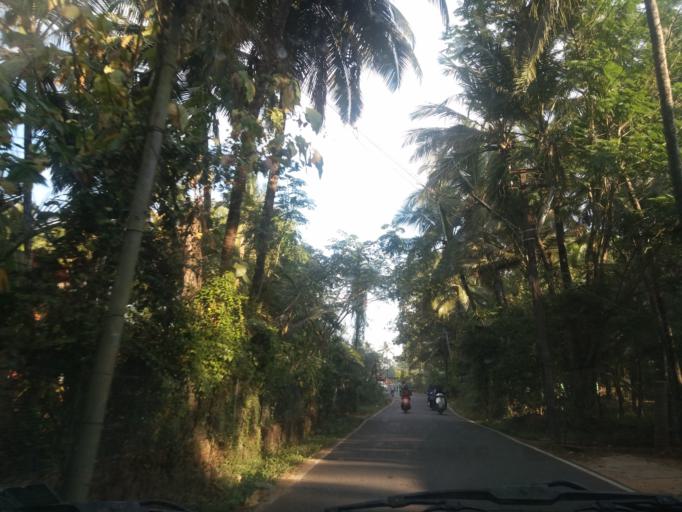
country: IN
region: Goa
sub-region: South Goa
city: Varca
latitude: 15.2467
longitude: 73.9570
